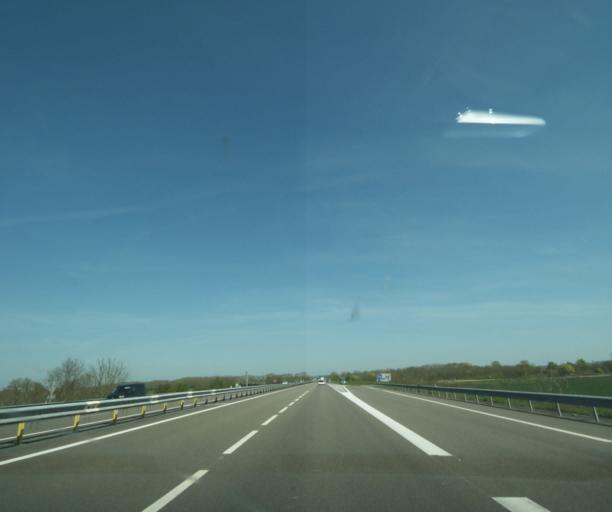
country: FR
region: Bourgogne
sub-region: Departement de la Nievre
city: Sermoise-sur-Loire
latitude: 46.9543
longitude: 3.1707
